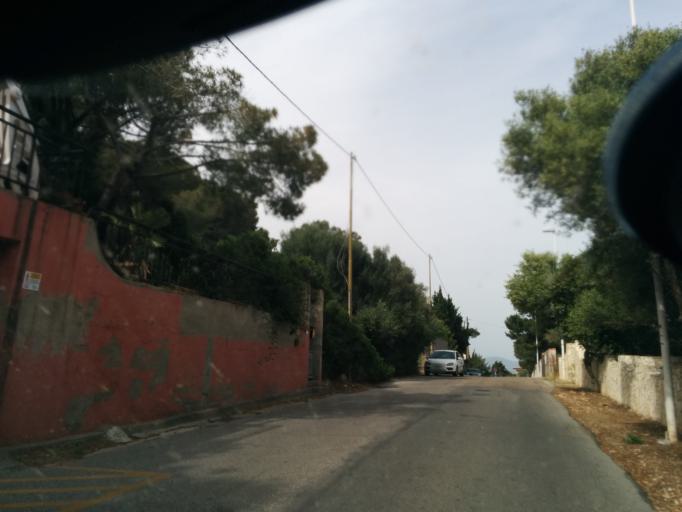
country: IT
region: Sardinia
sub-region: Provincia di Carbonia-Iglesias
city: Sant'Antioco
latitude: 39.0010
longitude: 8.4482
